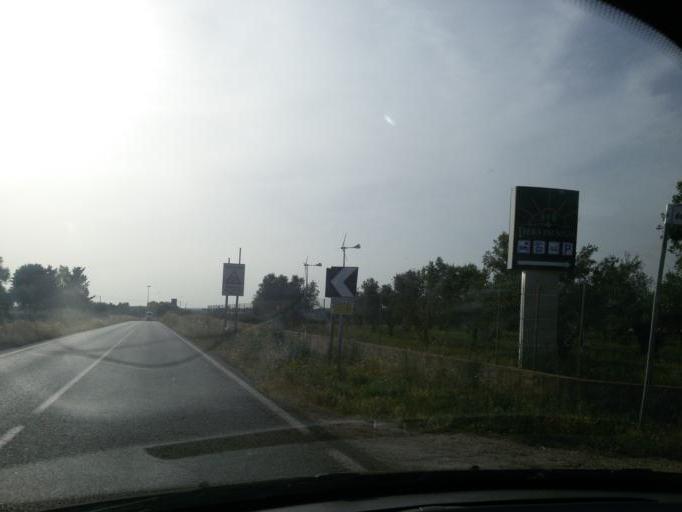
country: IT
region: Apulia
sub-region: Provincia di Lecce
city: Porto Cesareo
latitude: 40.2873
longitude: 17.8777
